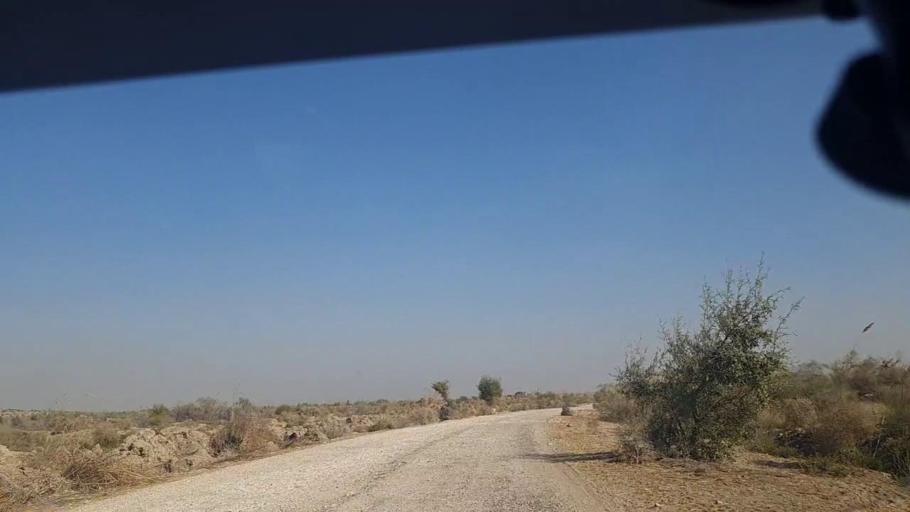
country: PK
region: Sindh
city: Khanpur
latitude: 27.5638
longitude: 69.3193
